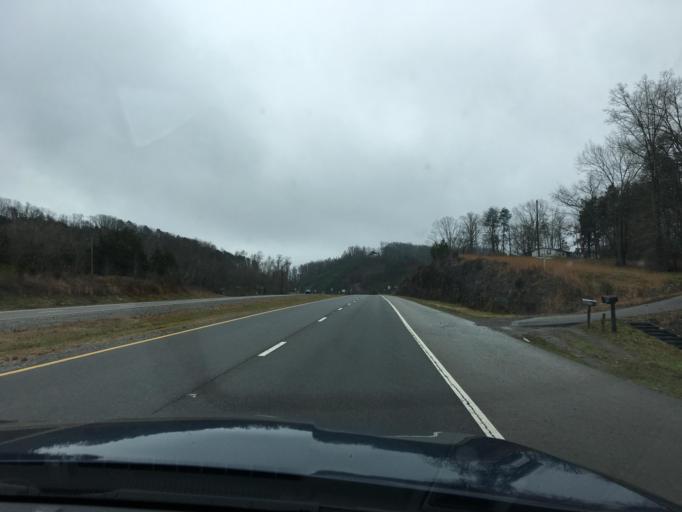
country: US
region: Tennessee
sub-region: McMinn County
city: Athens
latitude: 35.4150
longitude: -84.5833
